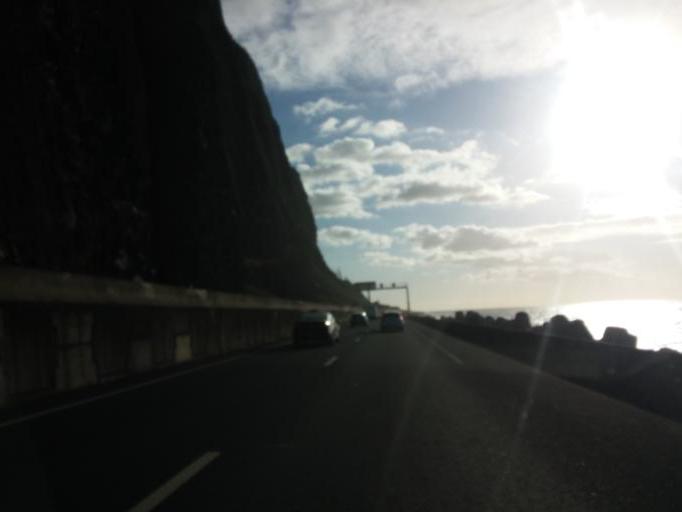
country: RE
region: Reunion
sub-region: Reunion
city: Saint-Denis
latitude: -20.8756
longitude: 55.4318
